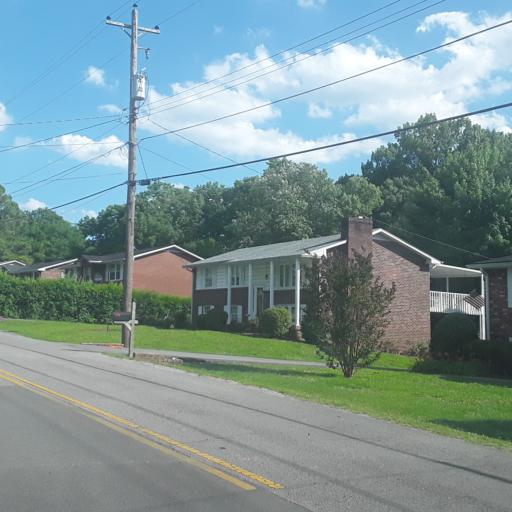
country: US
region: Tennessee
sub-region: Davidson County
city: Lakewood
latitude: 36.2049
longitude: -86.6375
